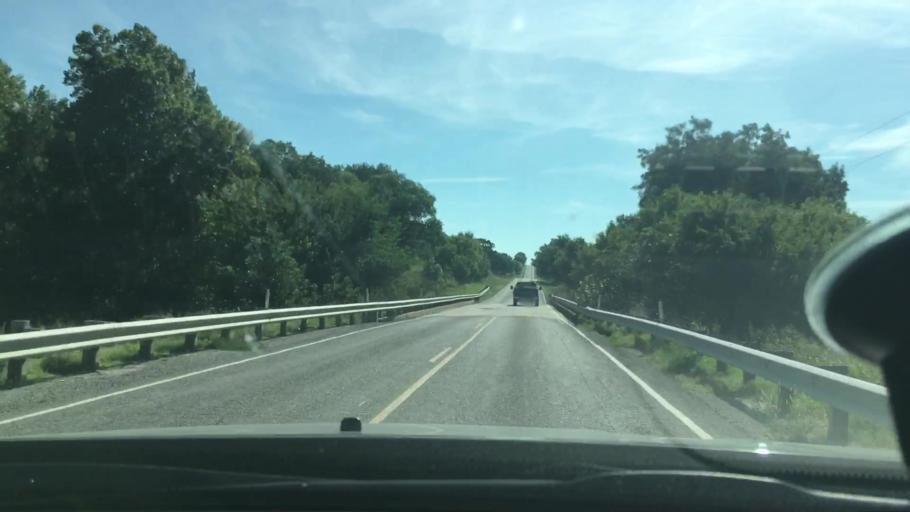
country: US
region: Oklahoma
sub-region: Carter County
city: Lone Grove
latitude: 34.3327
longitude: -97.2334
